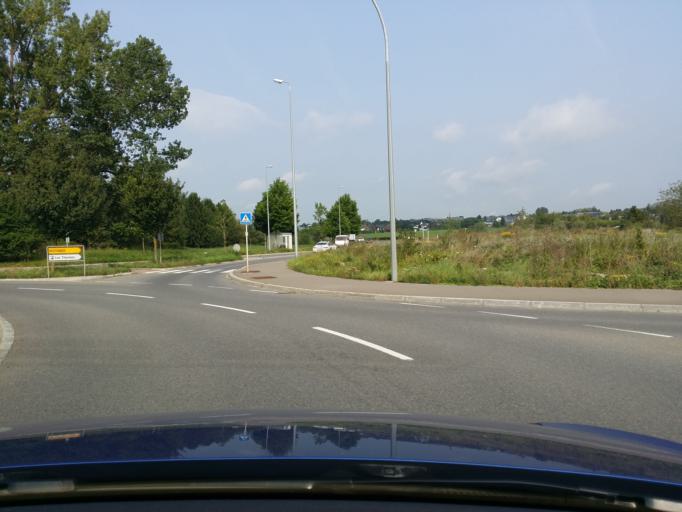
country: LU
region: Luxembourg
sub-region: Canton de Luxembourg
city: Strassen
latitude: 49.6108
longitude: 6.0715
